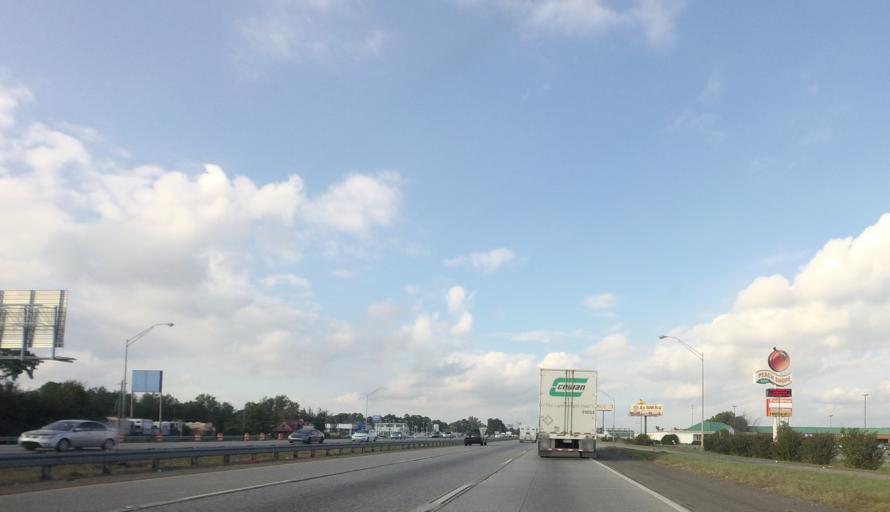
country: US
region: Georgia
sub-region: Peach County
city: Byron
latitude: 32.6616
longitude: -83.7442
